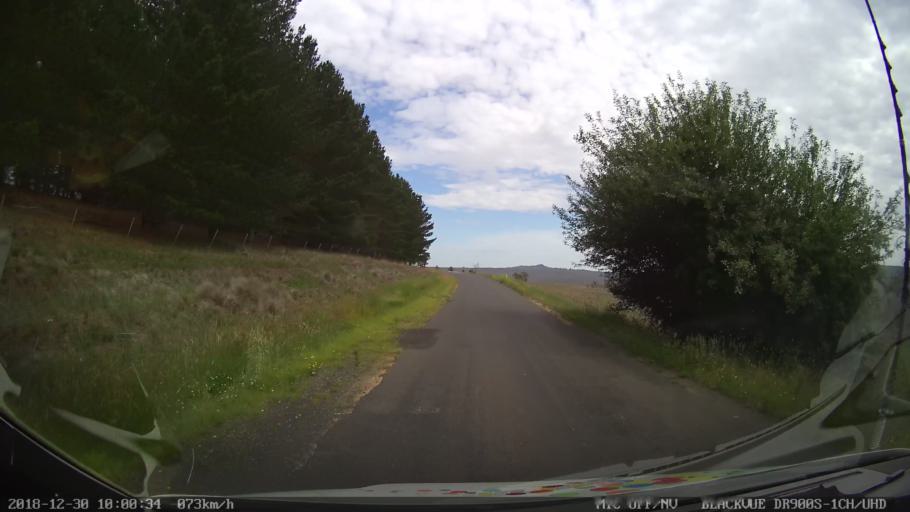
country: AU
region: New South Wales
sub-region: Cooma-Monaro
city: Cooma
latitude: -36.5154
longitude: 149.1972
